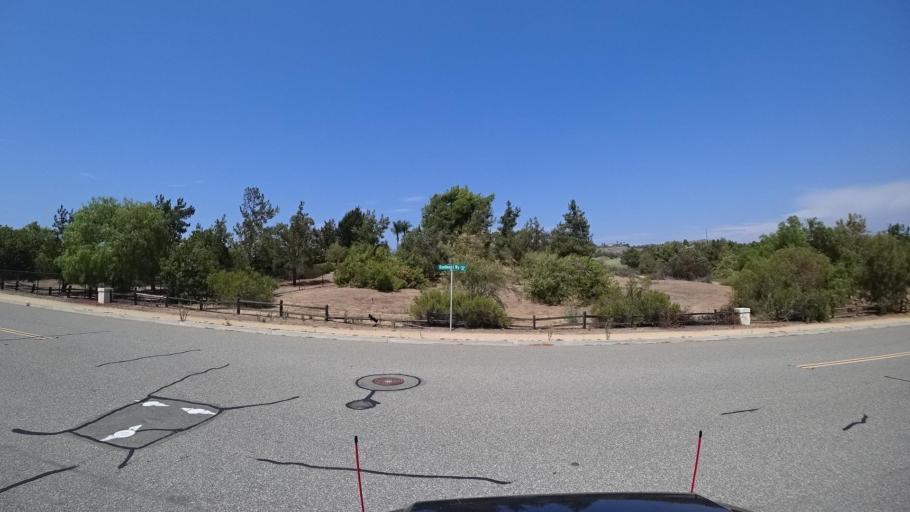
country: US
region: California
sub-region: San Diego County
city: Bonsall
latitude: 33.3237
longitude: -117.2036
